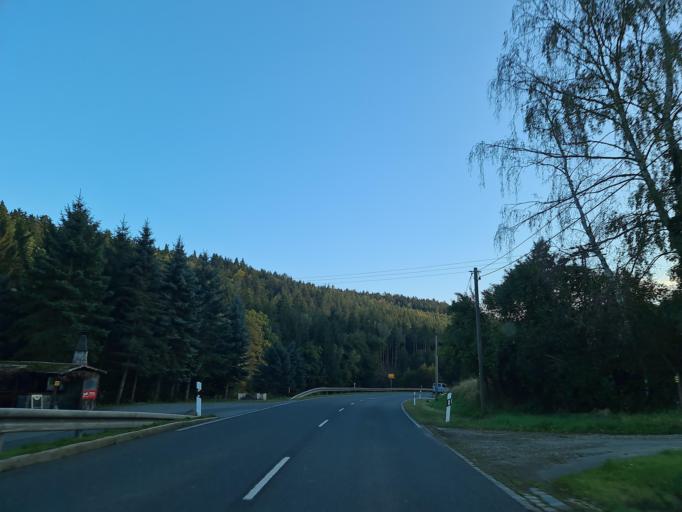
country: DE
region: Saxony
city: Elsterberg
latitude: 50.5892
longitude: 12.1377
